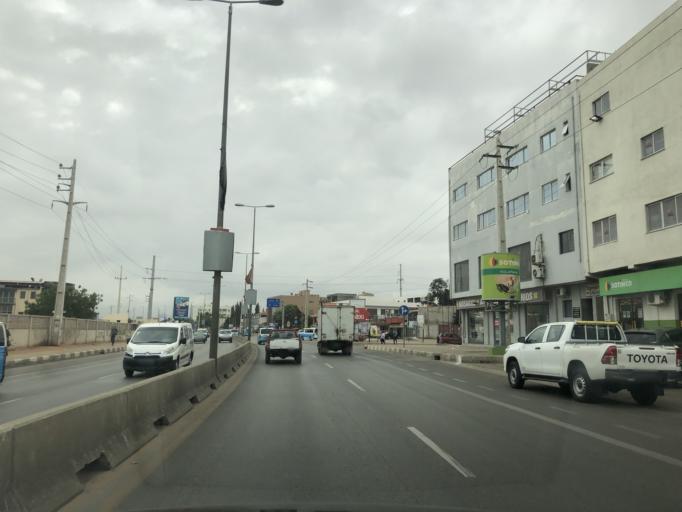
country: AO
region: Luanda
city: Luanda
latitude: -8.8947
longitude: 13.1930
